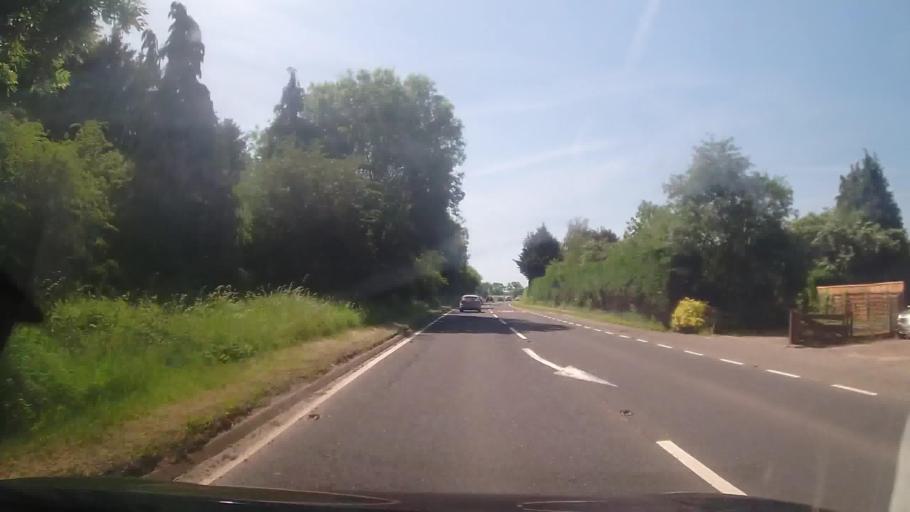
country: GB
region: England
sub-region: Herefordshire
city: Dinmore
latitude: 52.1470
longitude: -2.7275
